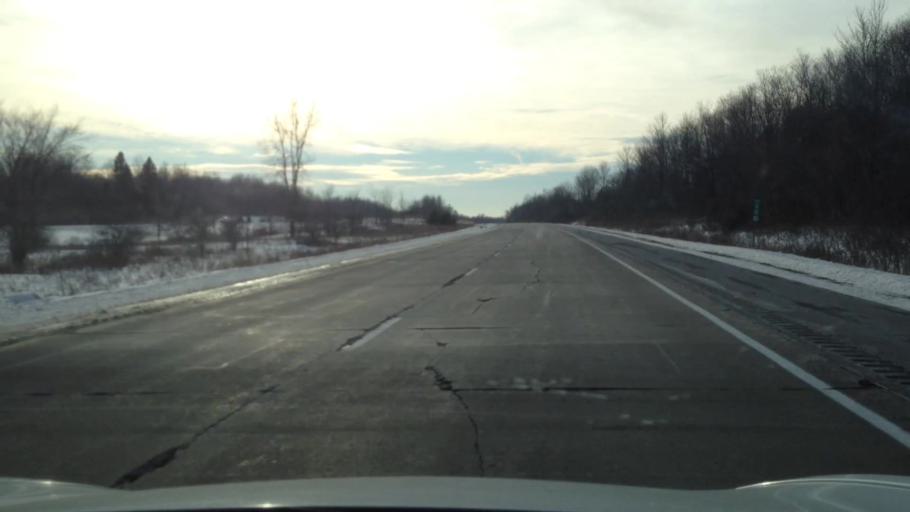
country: CA
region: Ontario
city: Hawkesbury
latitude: 45.5024
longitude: -74.5962
